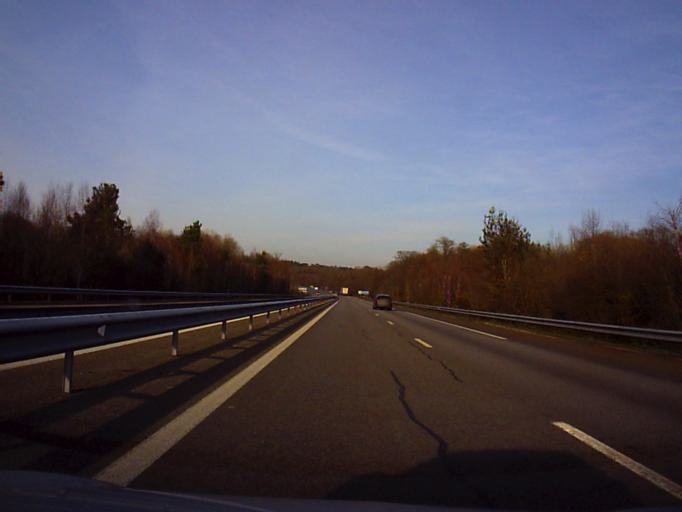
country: FR
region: Brittany
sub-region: Departement du Morbihan
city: Guer
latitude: 47.9441
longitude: -2.1026
